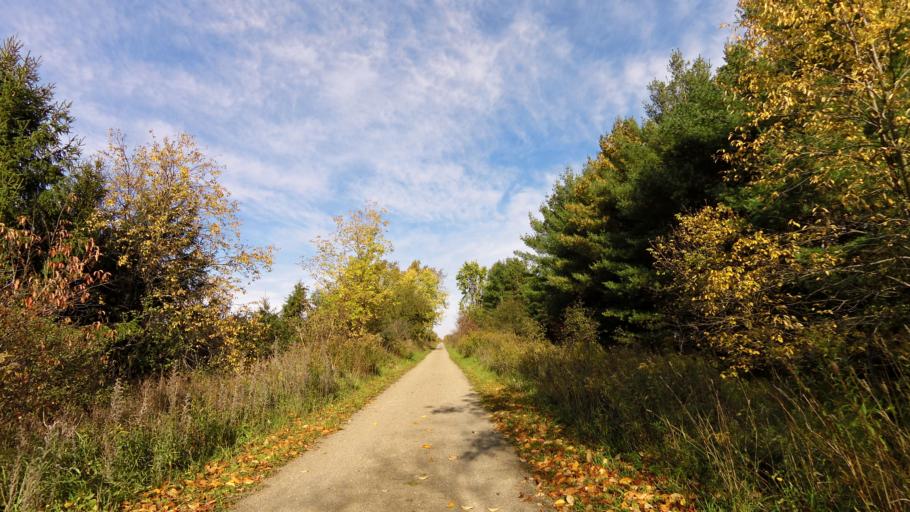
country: CA
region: Ontario
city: Orangeville
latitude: 43.7895
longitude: -80.0519
